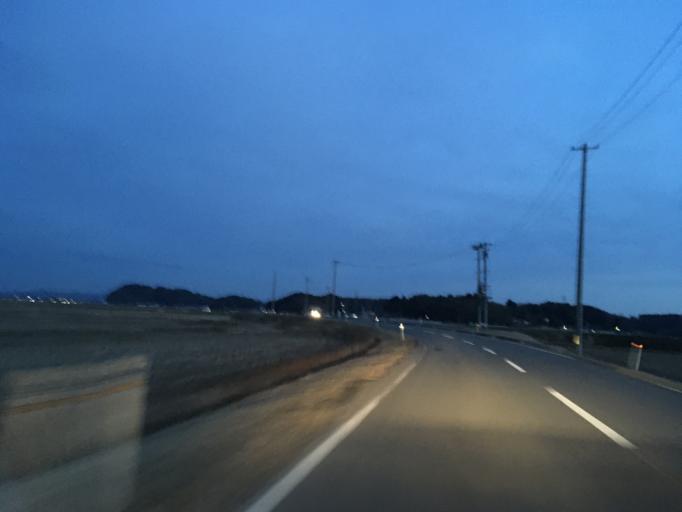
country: JP
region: Miyagi
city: Wakuya
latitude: 38.7107
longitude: 141.1507
